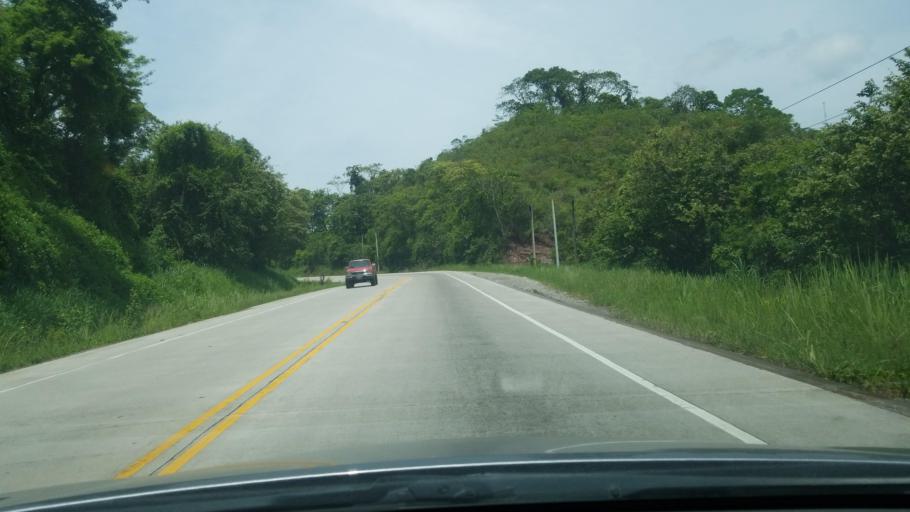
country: HN
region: Copan
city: Agua Caliente
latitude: 14.8669
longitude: -88.7864
